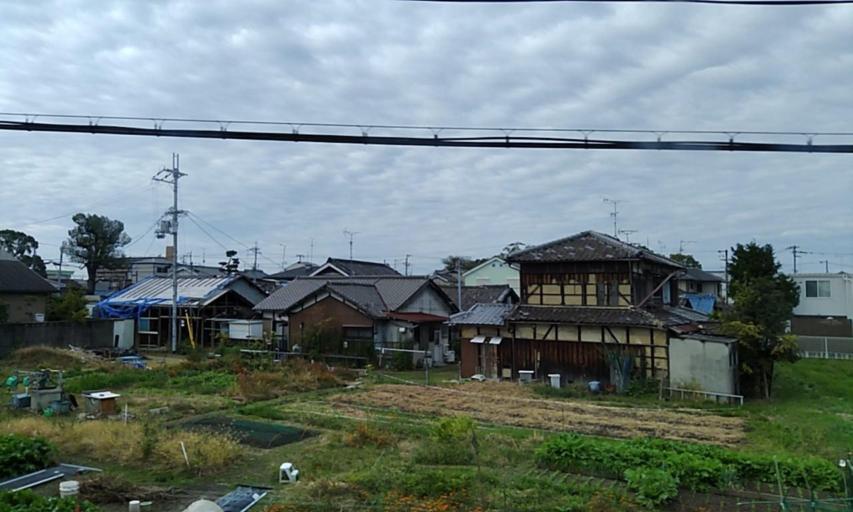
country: JP
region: Osaka
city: Matsubara
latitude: 34.5796
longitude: 135.5385
